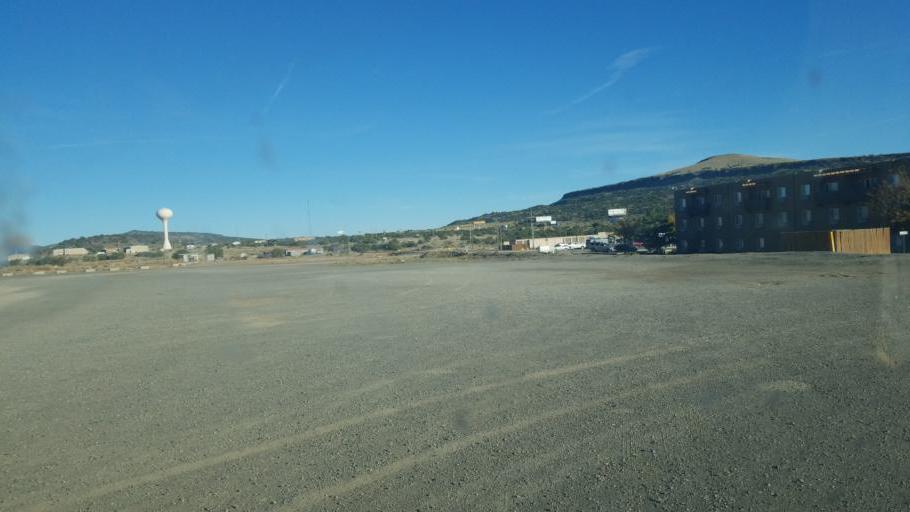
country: US
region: New Mexico
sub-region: Cibola County
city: Skyline-Ganipa
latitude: 35.0774
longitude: -107.5562
